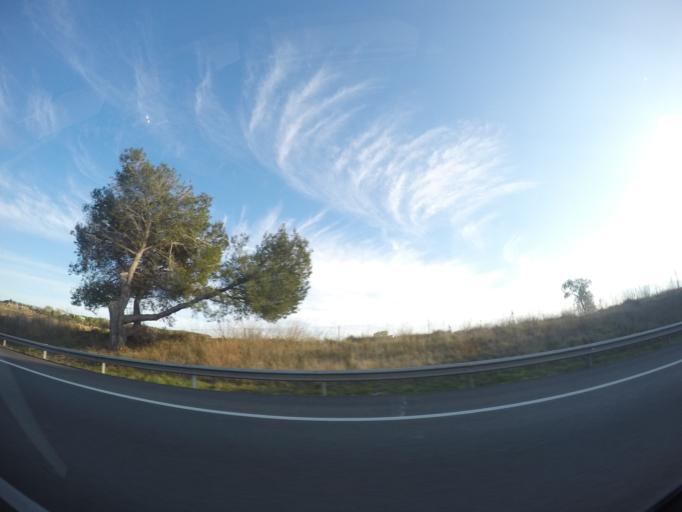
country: ES
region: Catalonia
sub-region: Provincia de Barcelona
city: Vilafranca del Penedes
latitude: 41.3292
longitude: 1.6994
